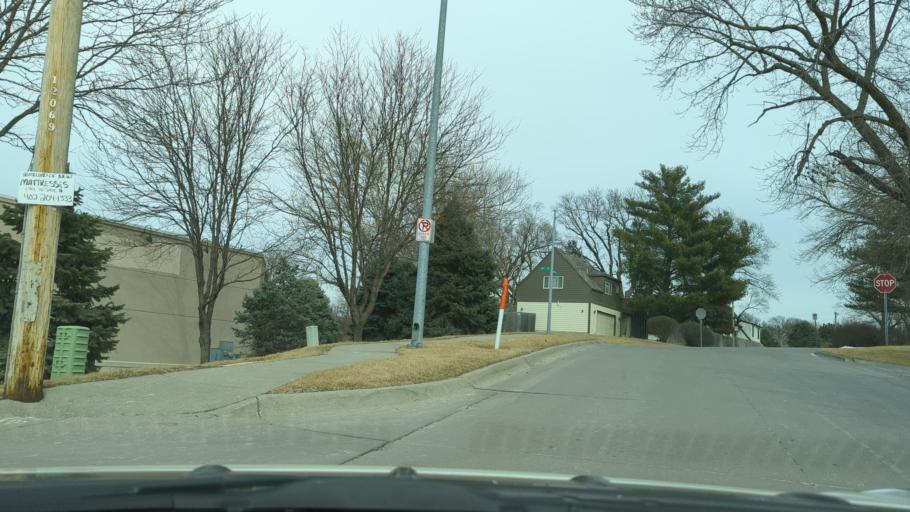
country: US
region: Nebraska
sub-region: Douglas County
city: Ralston
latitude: 41.2581
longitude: -96.0234
